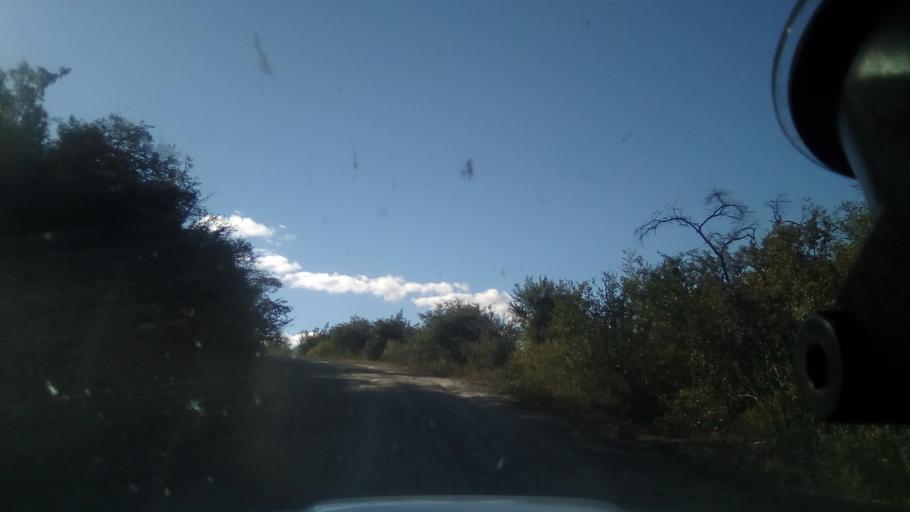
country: ZA
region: Eastern Cape
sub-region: Buffalo City Metropolitan Municipality
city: Bhisho
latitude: -32.7376
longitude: 27.3482
